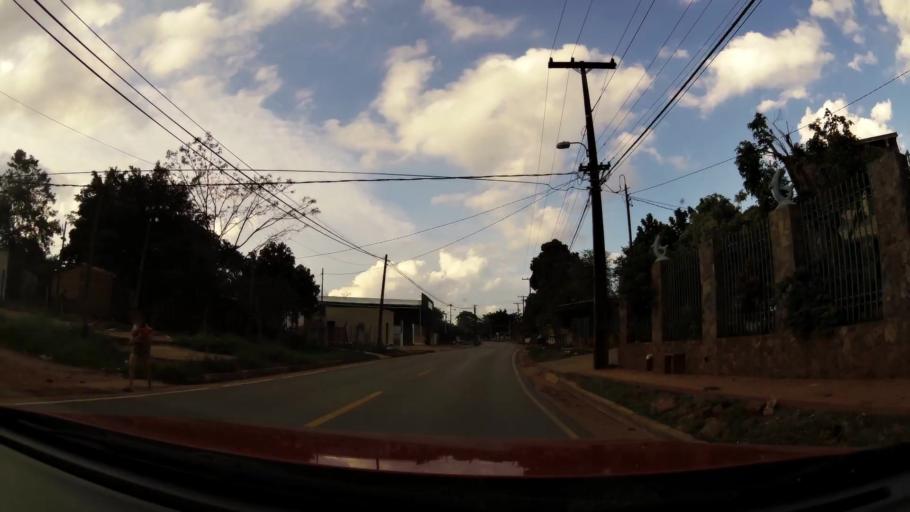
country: PY
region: Central
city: Nemby
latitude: -25.3710
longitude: -57.5432
